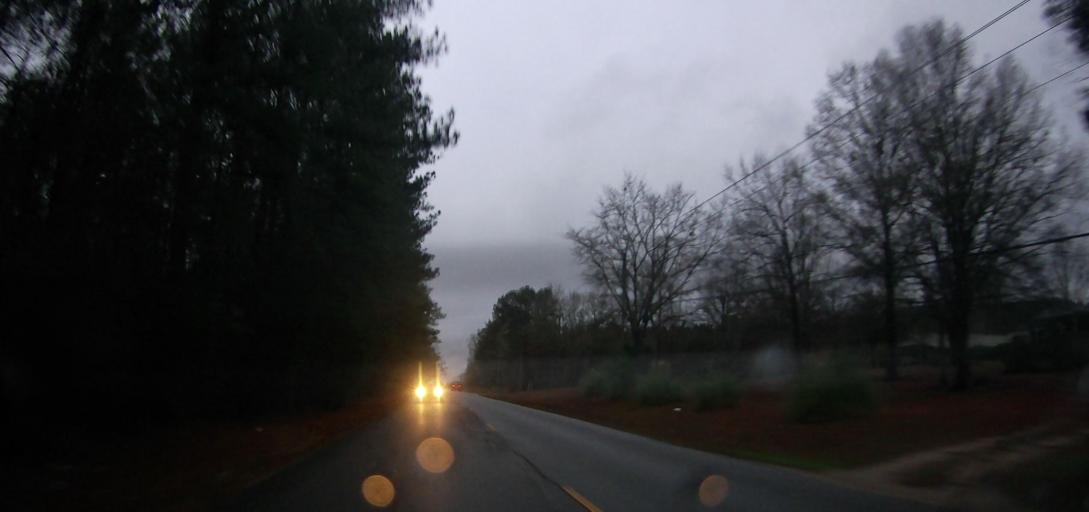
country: US
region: Alabama
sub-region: Tuscaloosa County
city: Vance
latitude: 33.1524
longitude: -87.2299
